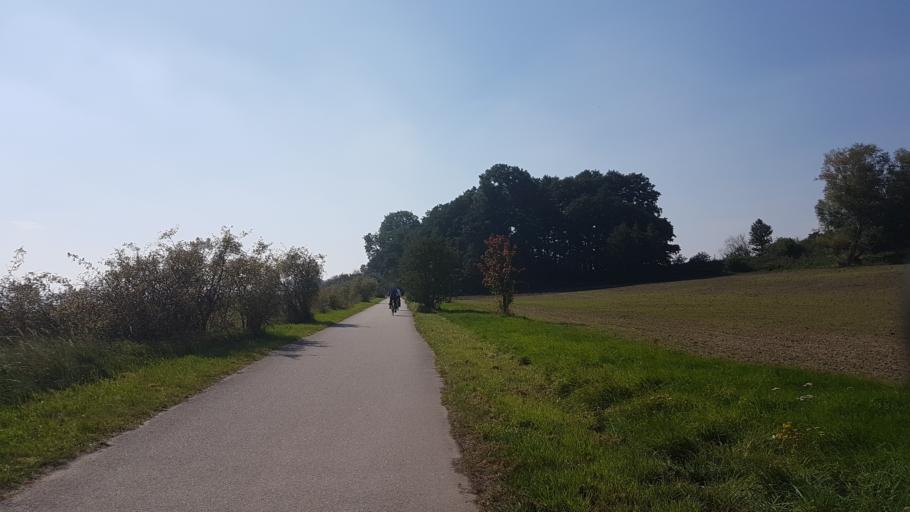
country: DE
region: Mecklenburg-Vorpommern
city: Ostseebad Binz
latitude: 54.3520
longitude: 13.5717
